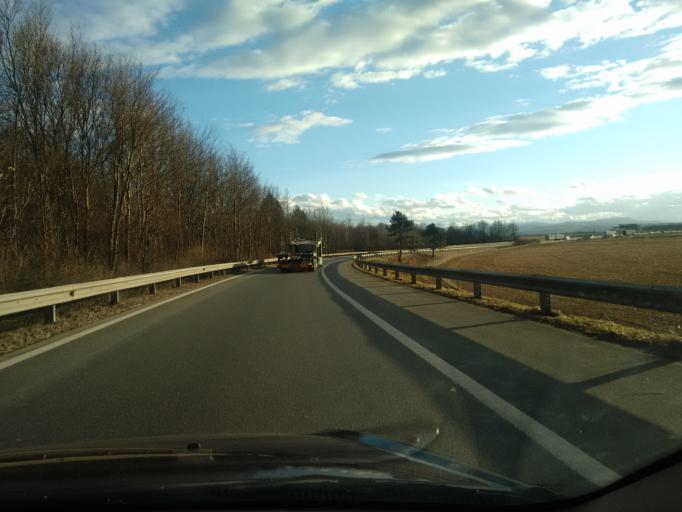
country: AT
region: Lower Austria
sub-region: Politischer Bezirk Sankt Polten
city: Pyhra
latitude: 48.1814
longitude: 15.6614
